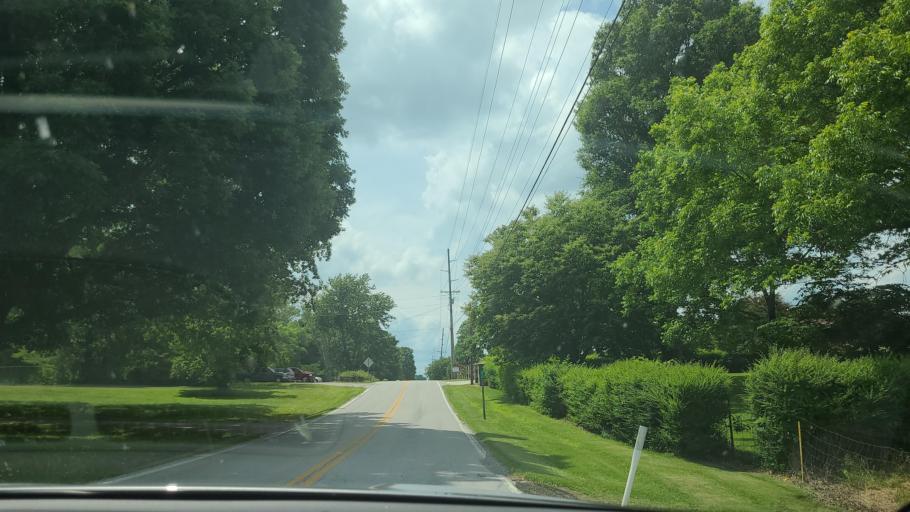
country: US
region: Tennessee
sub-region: Cumberland County
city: Crossville
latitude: 35.9056
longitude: -85.0045
